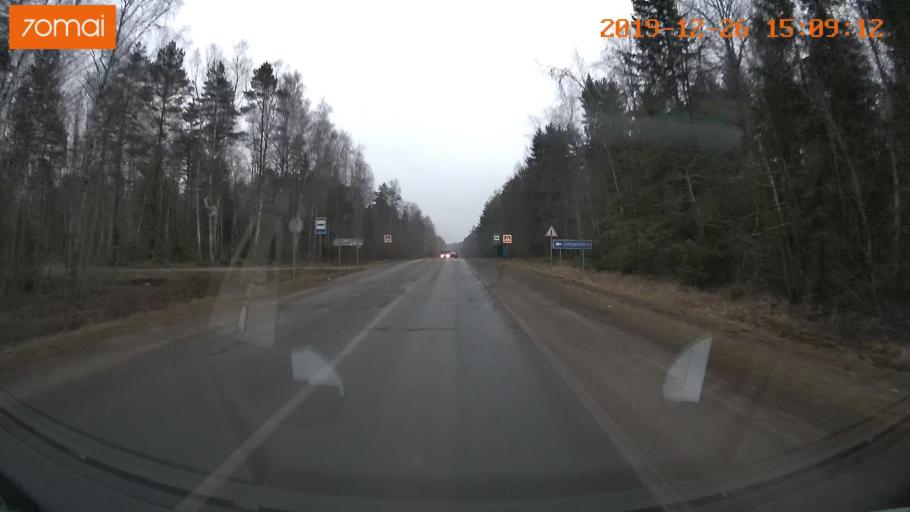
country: RU
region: Jaroslavl
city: Rybinsk
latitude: 58.1513
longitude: 38.8386
